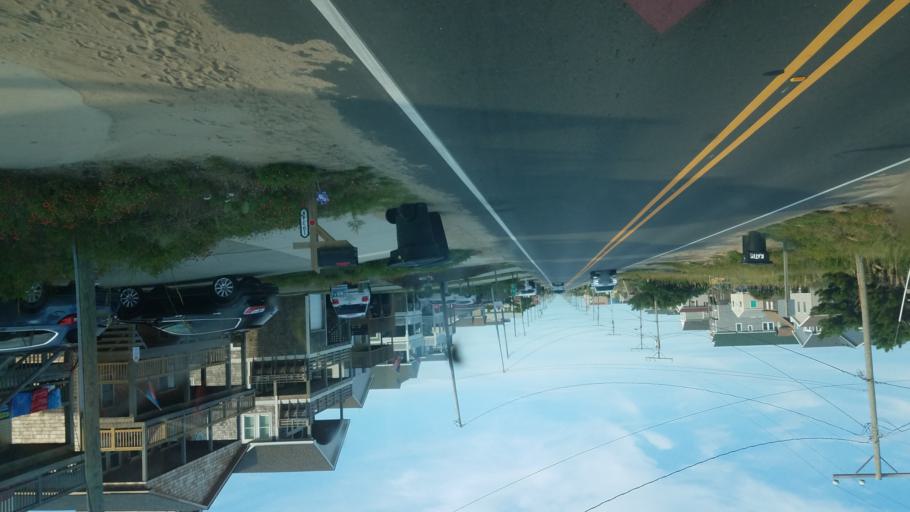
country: US
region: North Carolina
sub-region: Dare County
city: Kill Devil Hills
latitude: 36.0392
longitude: -75.6724
